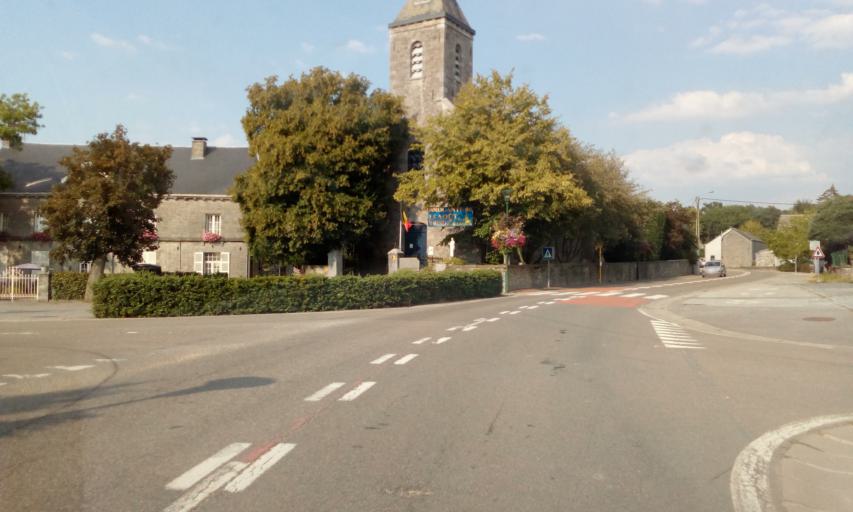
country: BE
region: Wallonia
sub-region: Province de Namur
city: Rochefort
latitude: 50.1209
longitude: 5.2483
